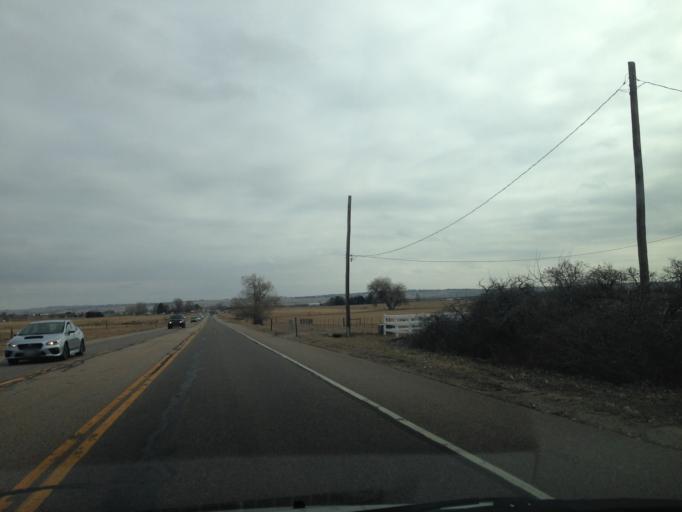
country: US
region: Colorado
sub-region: Boulder County
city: Louisville
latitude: 39.9579
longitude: -105.1383
